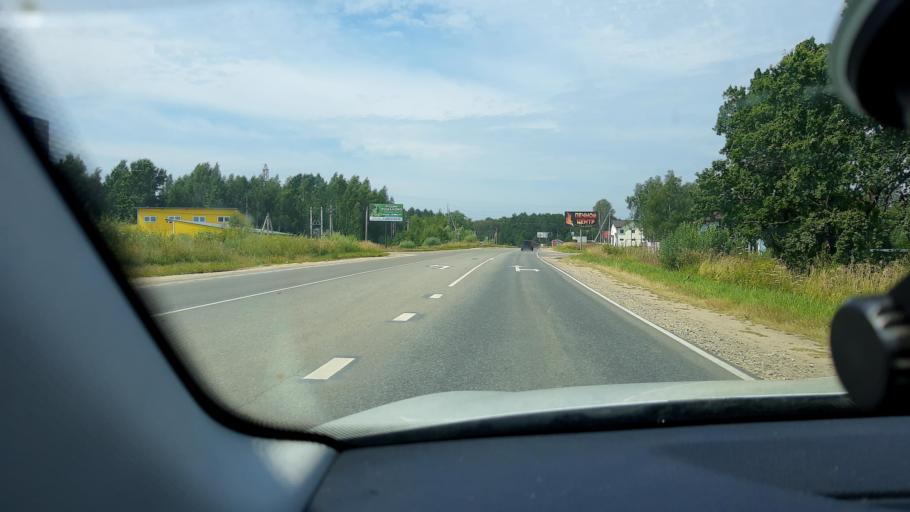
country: RU
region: Tula
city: Zaokskiy
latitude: 54.7461
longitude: 37.4097
